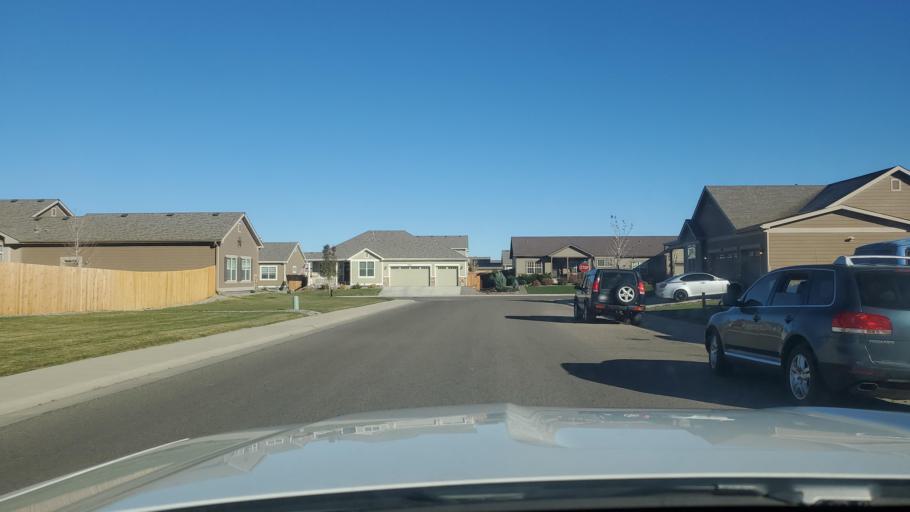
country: US
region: Colorado
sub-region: Adams County
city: Strasburg
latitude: 39.7497
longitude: -104.3262
